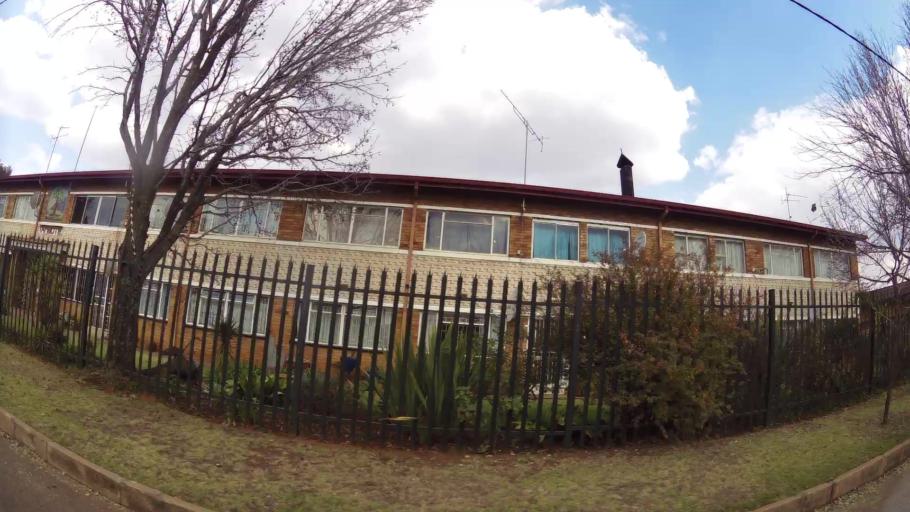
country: ZA
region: Mpumalanga
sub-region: Nkangala District Municipality
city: Delmas
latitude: -26.1478
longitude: 28.6833
